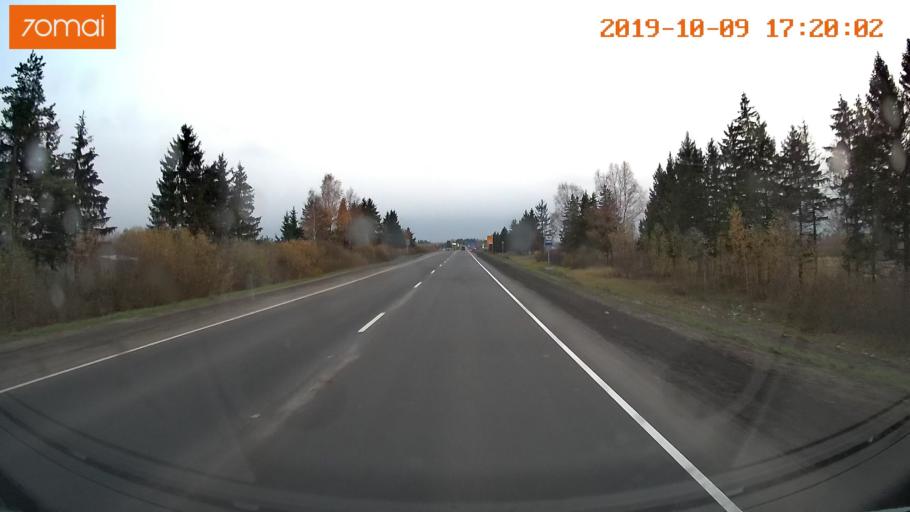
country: RU
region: Ivanovo
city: Furmanov
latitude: 57.2389
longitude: 41.1457
